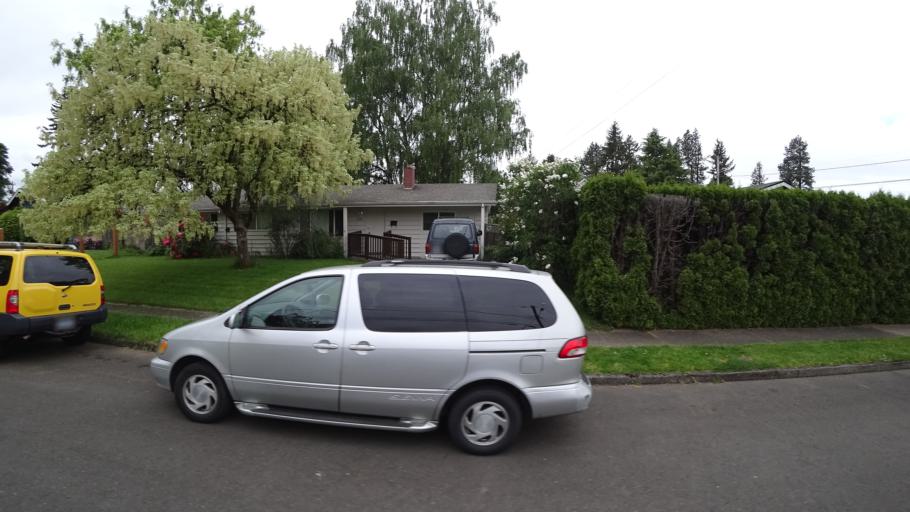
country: US
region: Oregon
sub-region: Washington County
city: Beaverton
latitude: 45.4786
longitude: -122.8016
